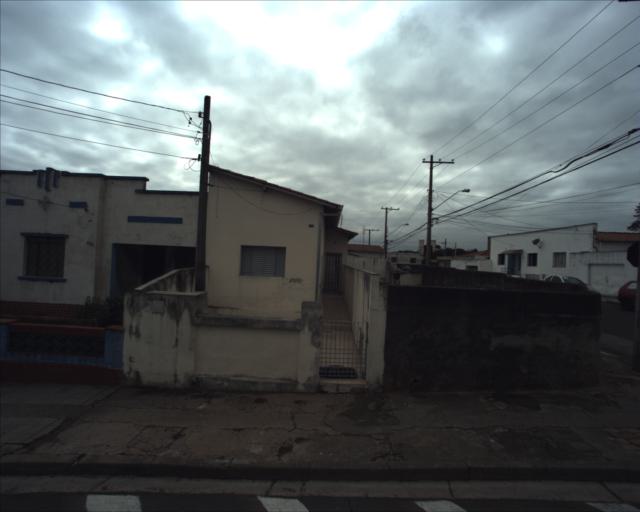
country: BR
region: Sao Paulo
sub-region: Sorocaba
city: Sorocaba
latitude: -23.4996
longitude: -47.4418
